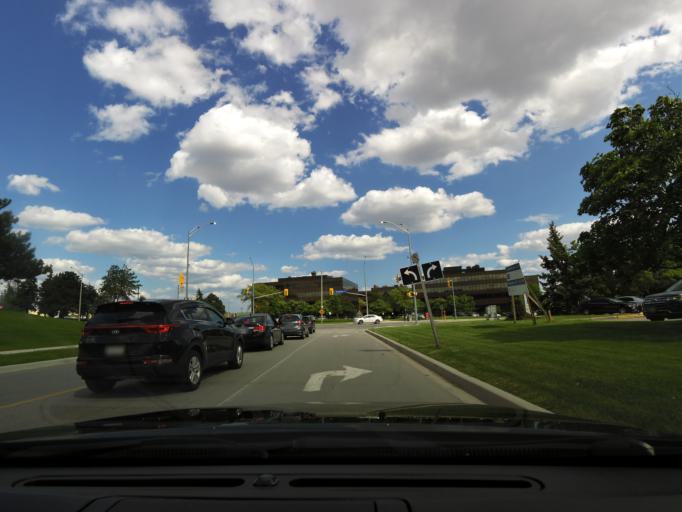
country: CA
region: Ontario
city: Brampton
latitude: 43.5997
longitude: -79.7428
